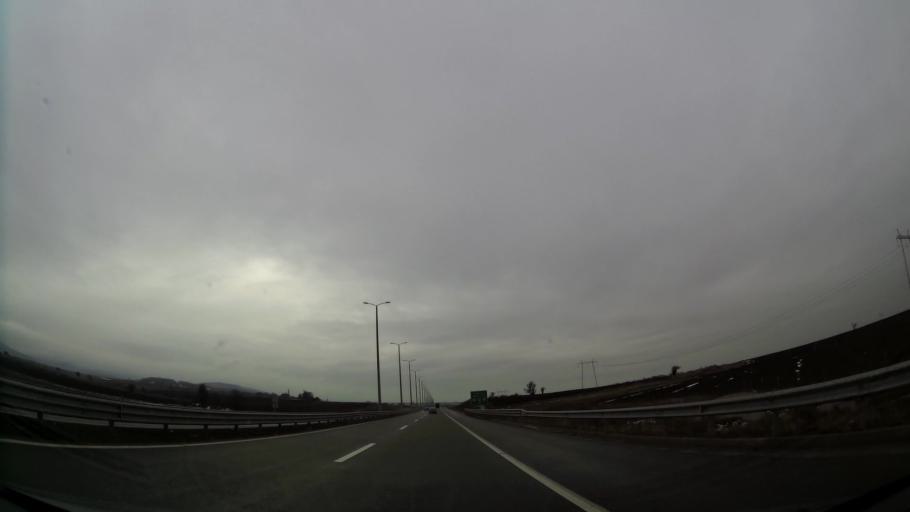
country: XK
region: Pristina
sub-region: Lipjan
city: Lipljan
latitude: 42.5001
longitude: 21.1861
